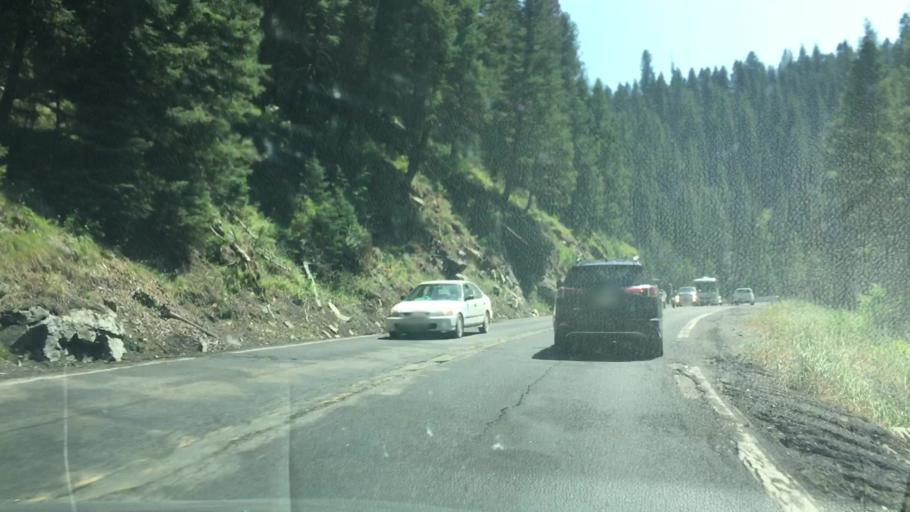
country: US
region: Idaho
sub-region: Valley County
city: McCall
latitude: 44.9629
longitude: -116.1737
